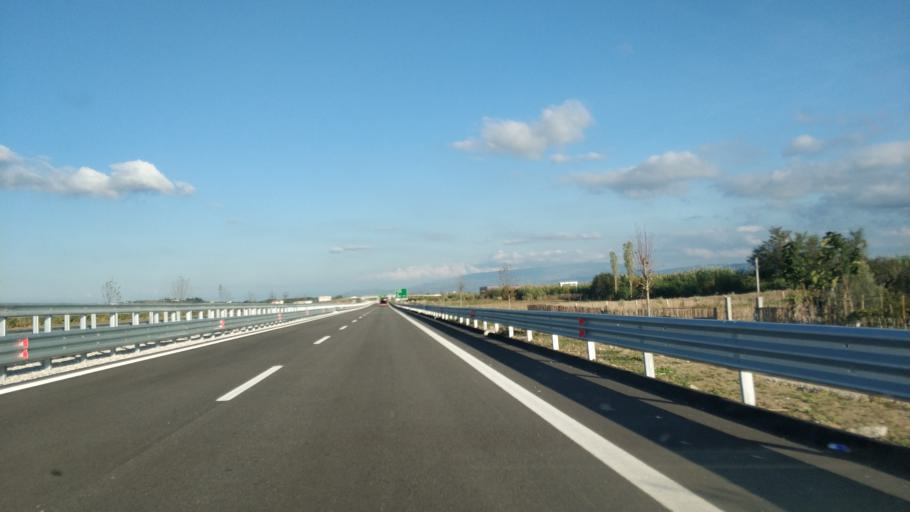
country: AL
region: Fier
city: Fier
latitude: 40.7493
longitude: 19.5464
